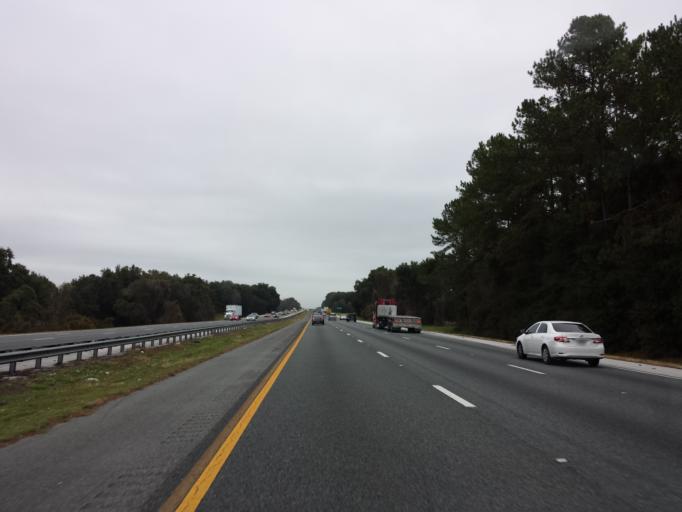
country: US
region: Florida
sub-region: Marion County
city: Ocala
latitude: 29.1057
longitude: -82.1848
